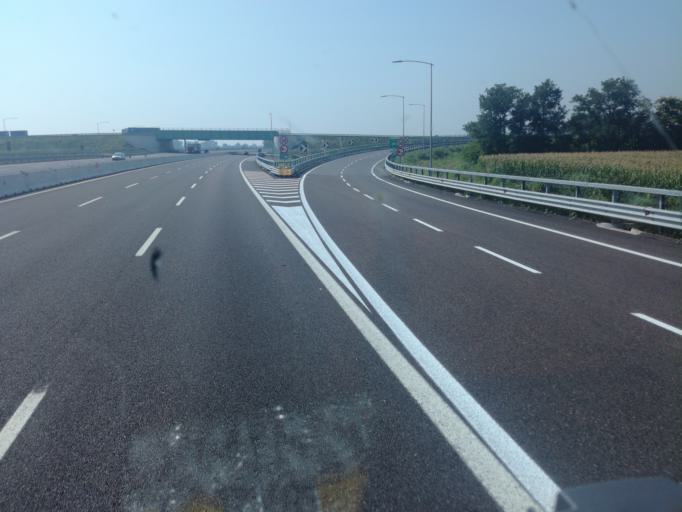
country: IT
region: Lombardy
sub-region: Citta metropolitana di Milano
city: Liscate
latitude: 45.4682
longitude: 9.4328
